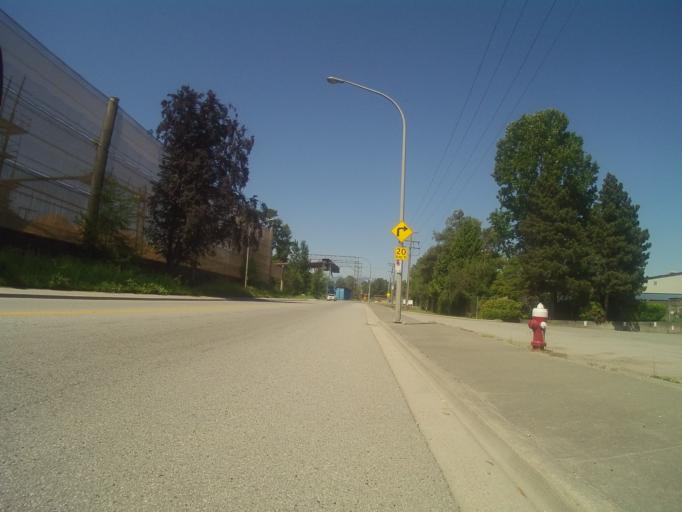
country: CA
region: British Columbia
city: Vancouver
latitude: 49.2003
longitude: -123.0692
